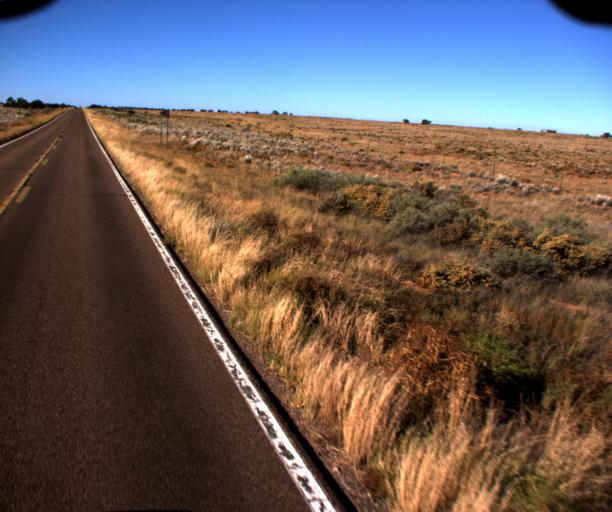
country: US
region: Arizona
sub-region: Navajo County
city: Snowflake
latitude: 34.6554
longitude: -110.3370
